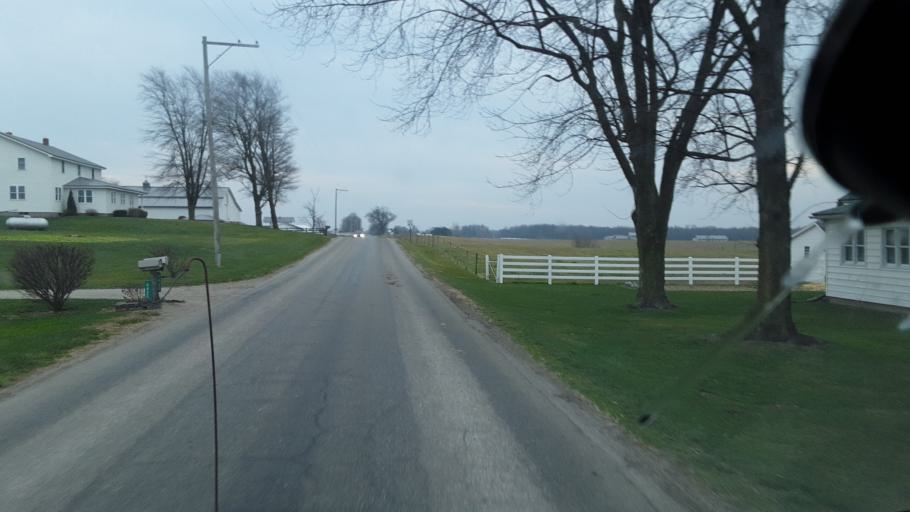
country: US
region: Indiana
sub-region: Elkhart County
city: Middlebury
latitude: 41.7037
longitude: -85.6202
